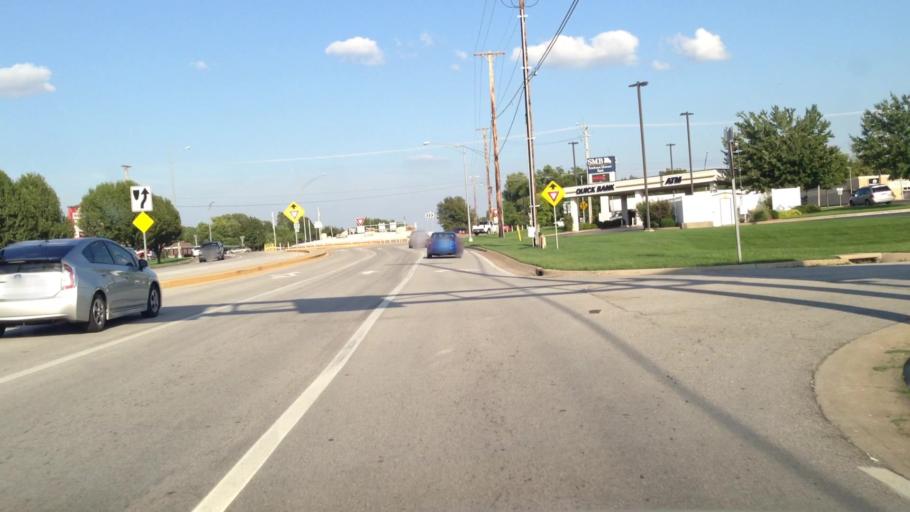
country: US
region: Missouri
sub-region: Jasper County
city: Webb City
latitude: 37.1428
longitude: -94.5134
